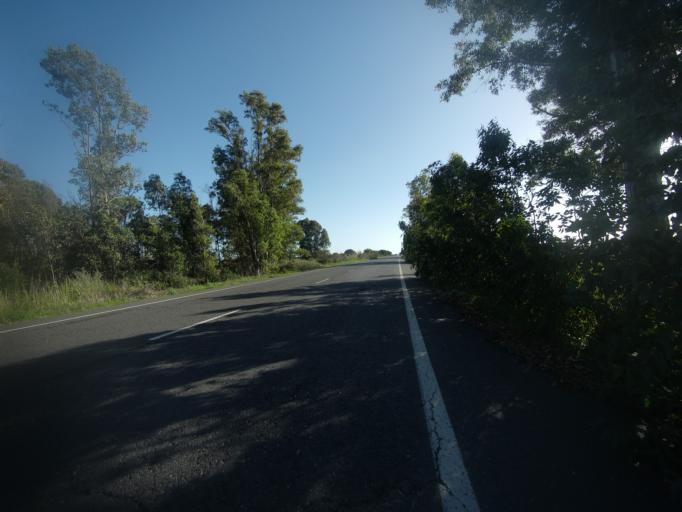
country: ES
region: Andalusia
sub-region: Provincia de Huelva
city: Huelva
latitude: 37.2382
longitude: -6.9649
